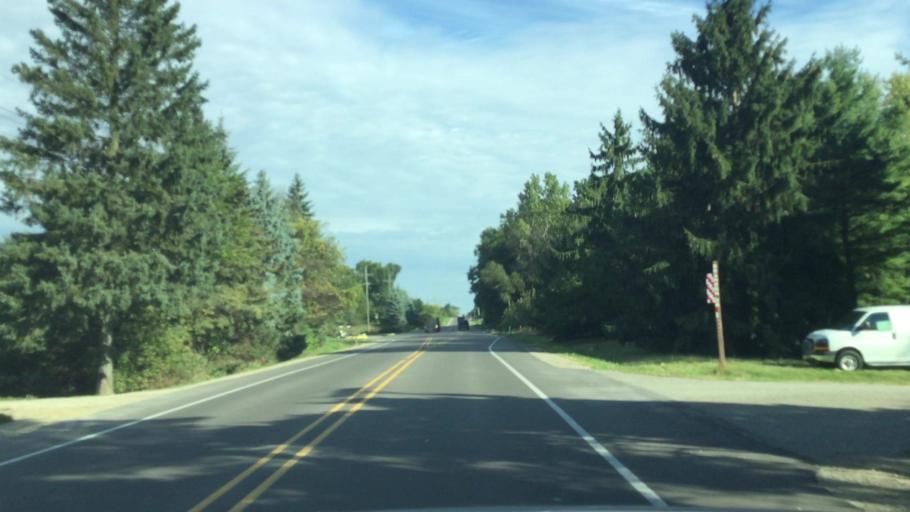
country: US
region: Michigan
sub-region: Livingston County
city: Howell
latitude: 42.6052
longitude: -83.8747
